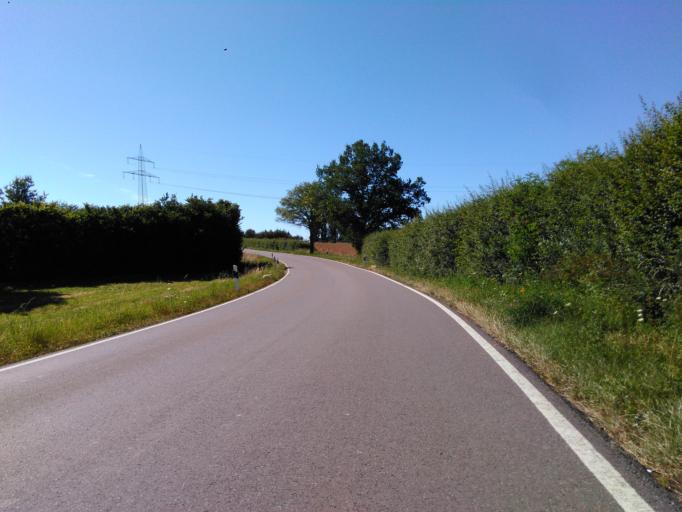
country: LU
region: Luxembourg
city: Schouweiler
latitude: 49.5723
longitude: 5.9654
